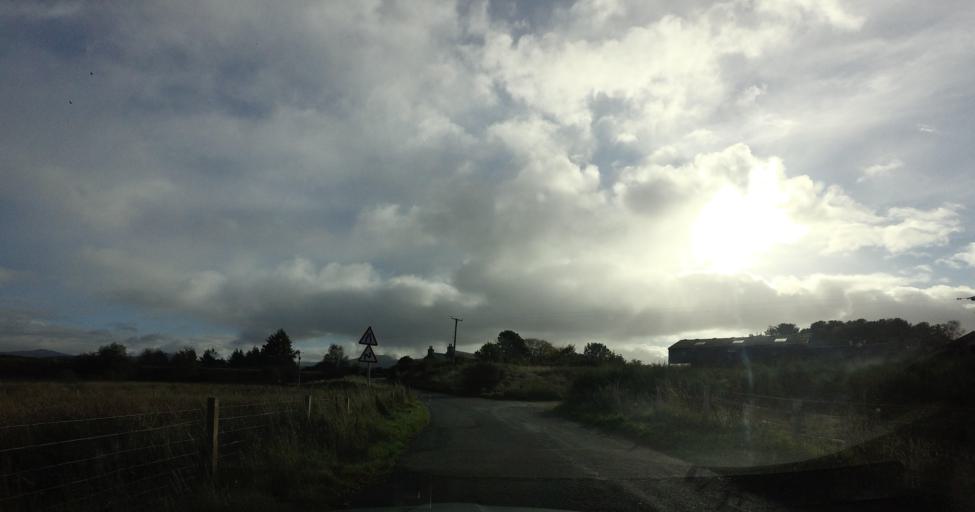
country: GB
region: Scotland
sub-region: Highland
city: Aviemore
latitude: 57.2550
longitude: -3.7509
